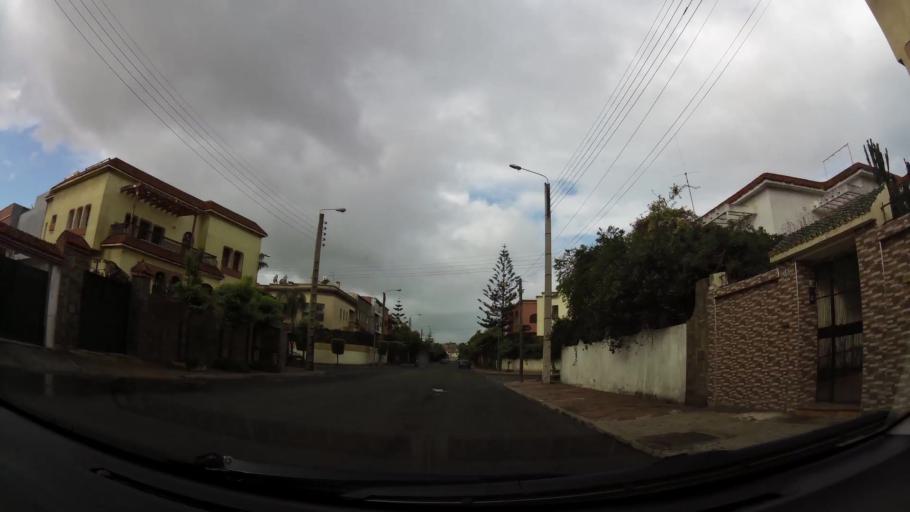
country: MA
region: Grand Casablanca
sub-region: Casablanca
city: Casablanca
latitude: 33.5637
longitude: -7.6764
